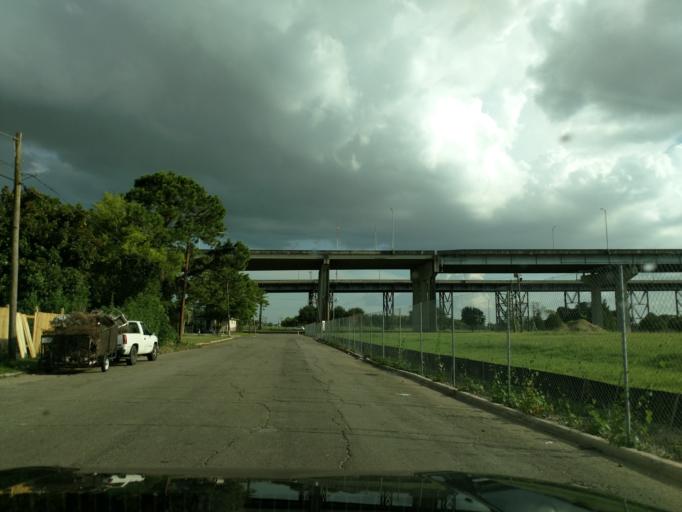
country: US
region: Louisiana
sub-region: Jefferson Parish
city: Gretna
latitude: 29.9400
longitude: -90.0435
